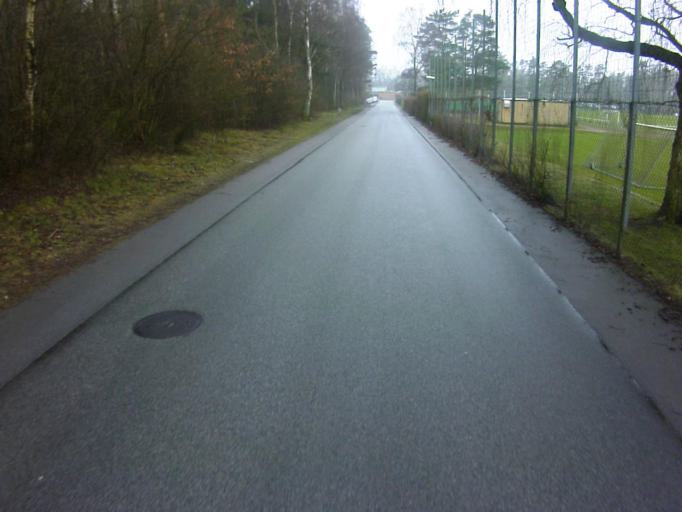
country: SE
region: Skane
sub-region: Kavlinge Kommun
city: Kaevlinge
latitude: 55.7771
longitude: 13.0879
